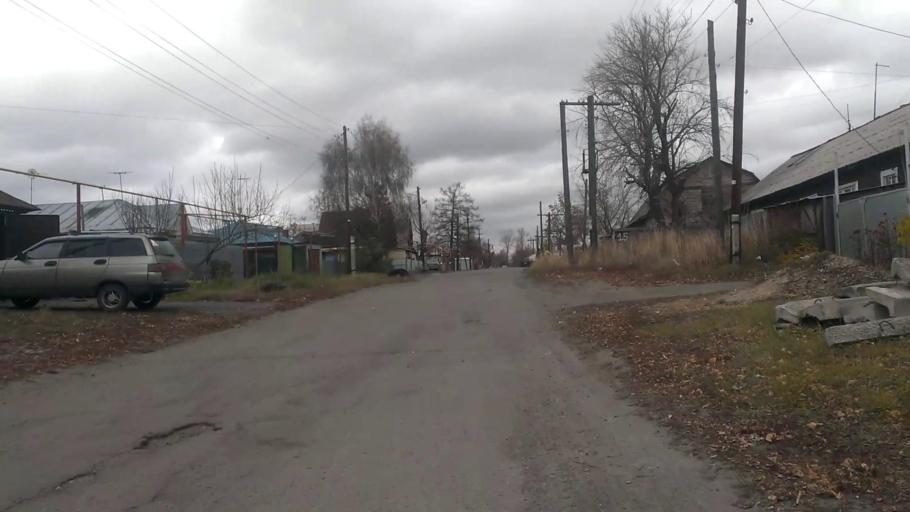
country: RU
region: Altai Krai
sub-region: Gorod Barnaulskiy
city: Barnaul
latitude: 53.3514
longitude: 83.7522
